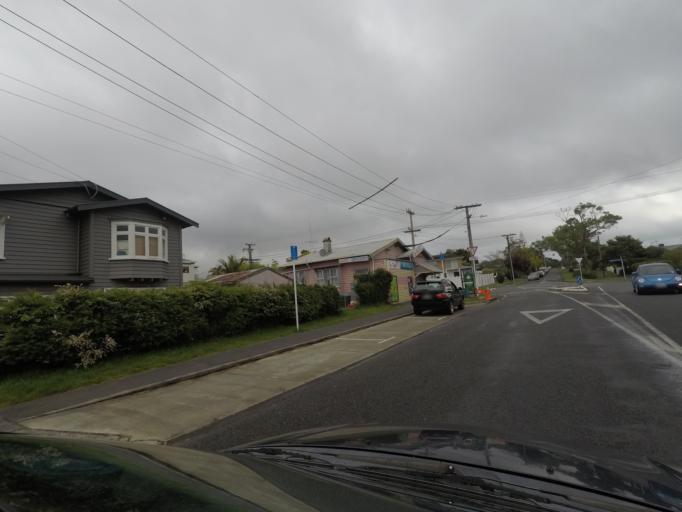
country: NZ
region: Auckland
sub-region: Auckland
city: Auckland
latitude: -36.8906
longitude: 174.7317
